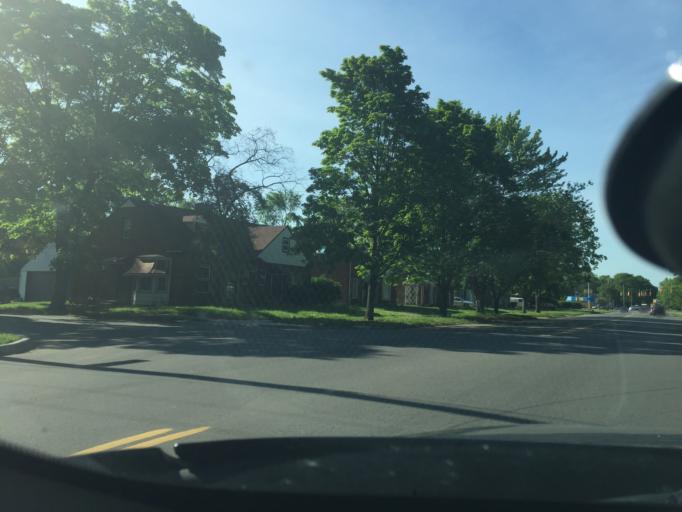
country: US
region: Michigan
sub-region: Oakland County
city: Southfield
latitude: 42.4131
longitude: -83.2380
